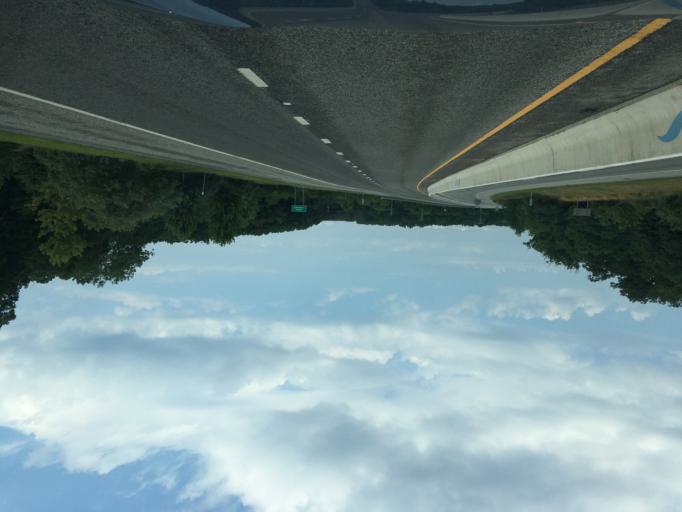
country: US
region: Rhode Island
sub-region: Kent County
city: East Greenwich
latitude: 41.6263
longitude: -71.4762
